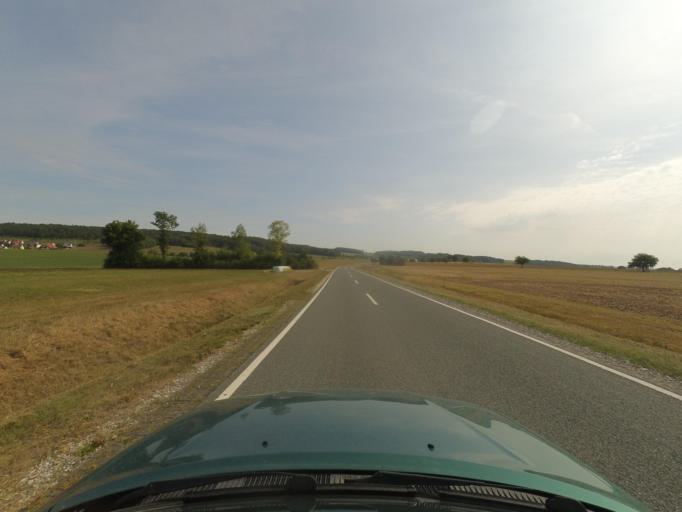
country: DE
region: Bavaria
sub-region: Regierungsbezirk Mittelfranken
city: Aurach
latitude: 49.1996
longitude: 10.4192
